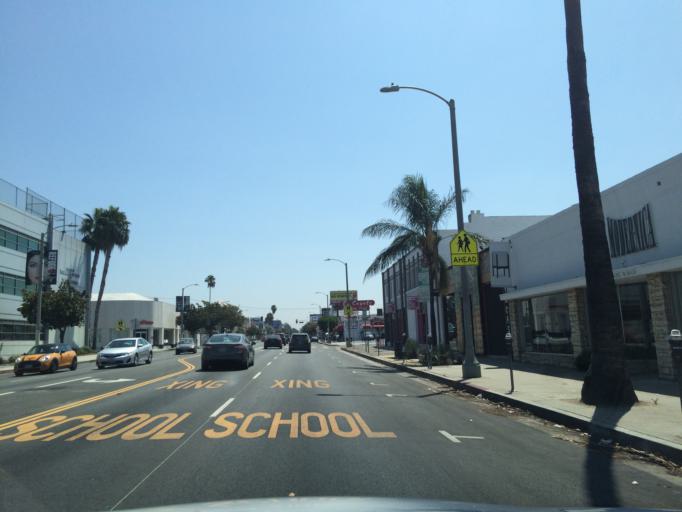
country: US
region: California
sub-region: Los Angeles County
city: West Hollywood
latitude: 34.0761
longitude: -118.3507
